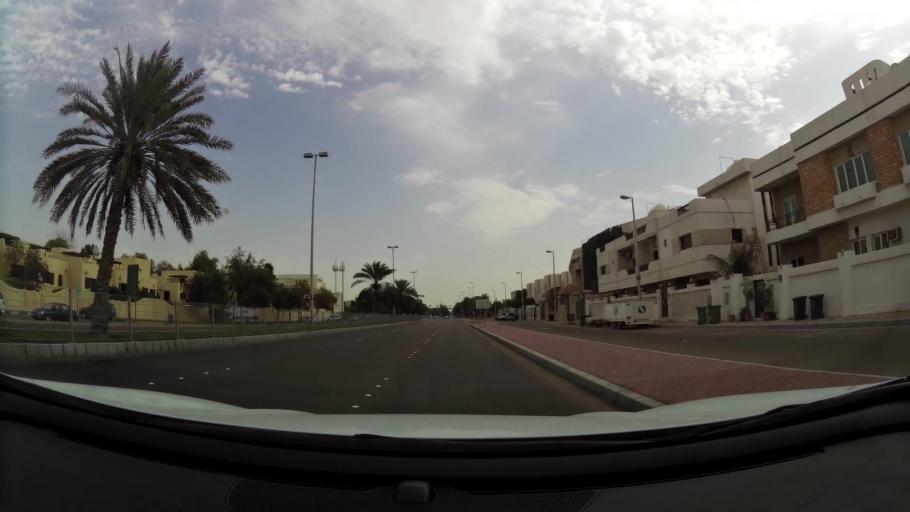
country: AE
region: Abu Dhabi
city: Abu Dhabi
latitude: 24.4607
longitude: 54.3708
